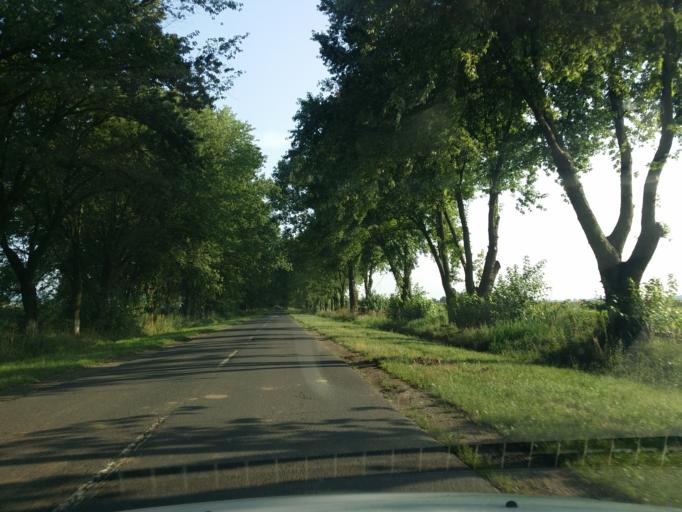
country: HU
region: Borsod-Abauj-Zemplen
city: Gonc
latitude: 48.4299
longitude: 21.2379
